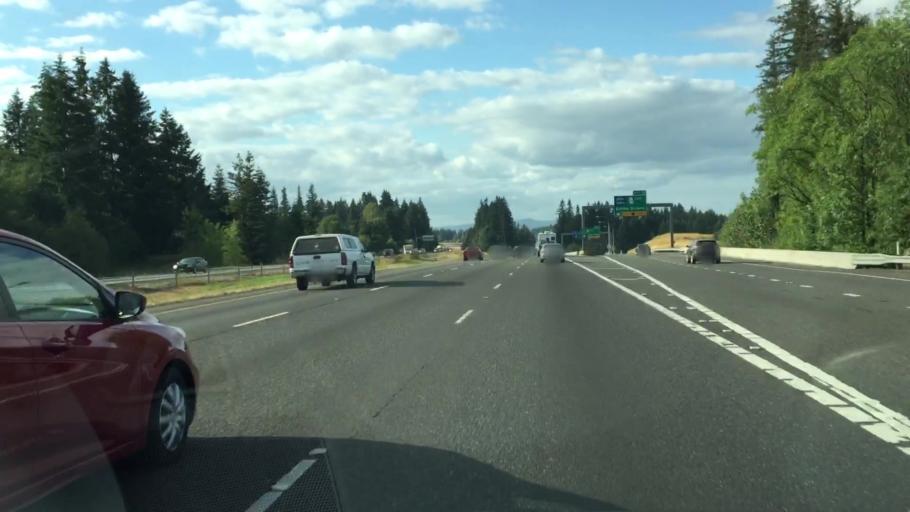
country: US
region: Washington
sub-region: Clark County
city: Mount Vista
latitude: 45.7684
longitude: -122.6682
